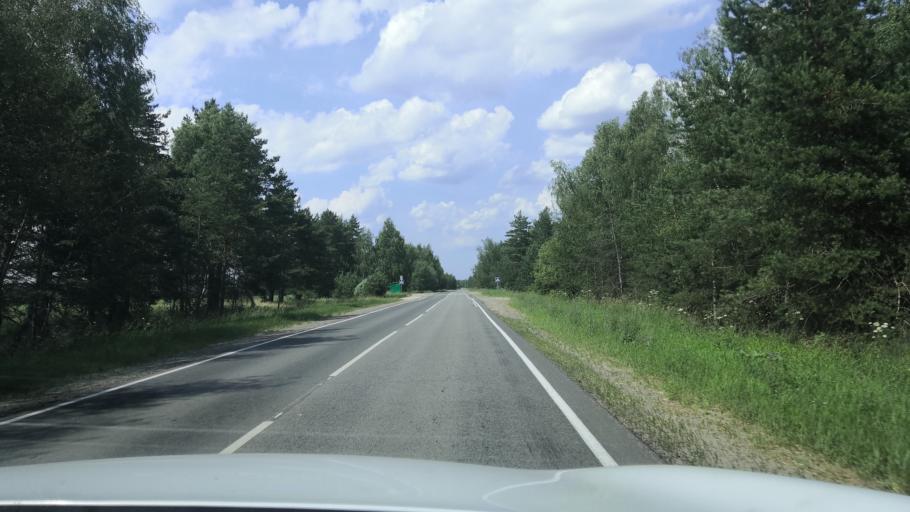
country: RU
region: Rjazan
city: Murmino
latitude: 54.5765
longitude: 40.1107
